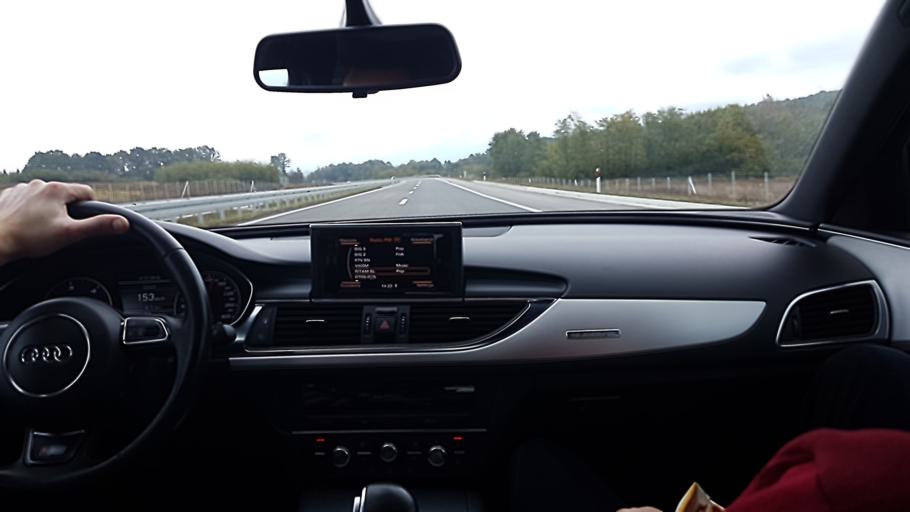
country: BA
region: Republika Srpska
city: Prnjavor
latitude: 44.8481
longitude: 17.7495
